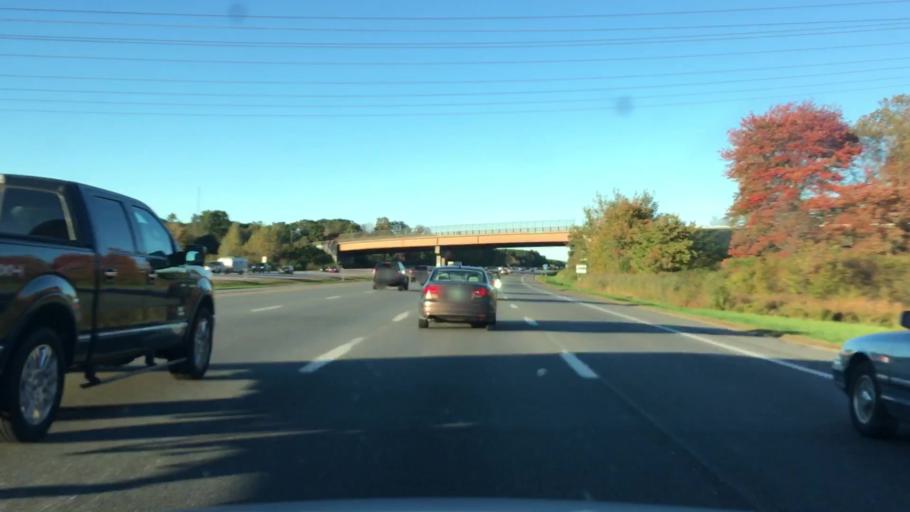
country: US
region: New Hampshire
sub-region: Rockingham County
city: North Hampton
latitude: 42.9922
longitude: -70.8493
